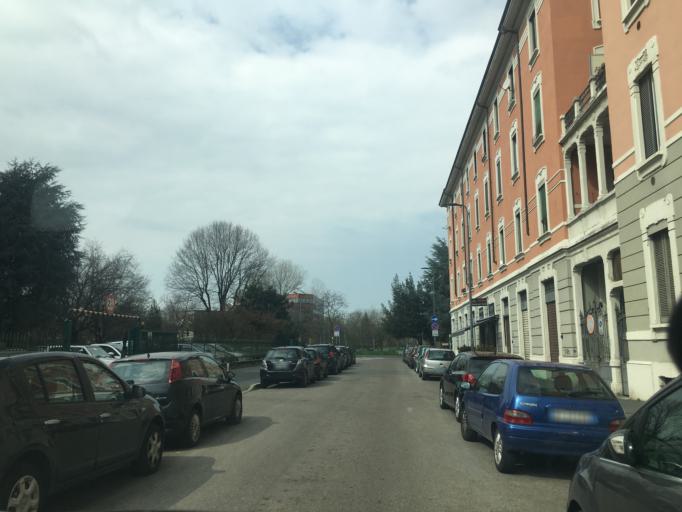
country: IT
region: Lombardy
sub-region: Citta metropolitana di Milano
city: Bresso
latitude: 45.5235
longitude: 9.2059
